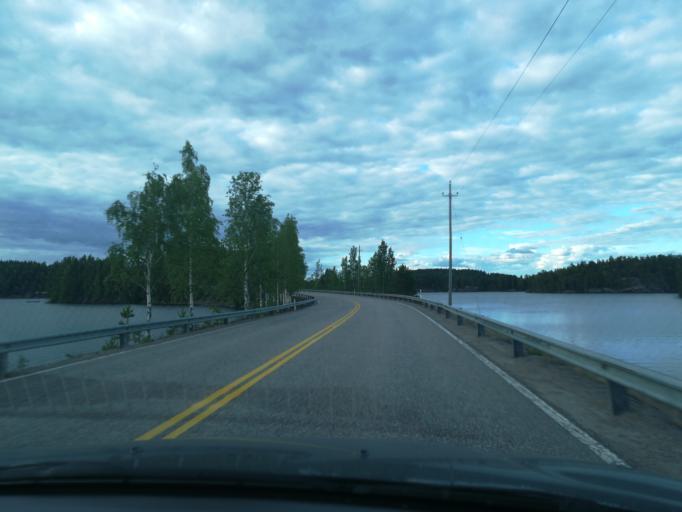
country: FI
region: Southern Savonia
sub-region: Mikkeli
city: Puumala
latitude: 61.5469
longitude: 27.9618
